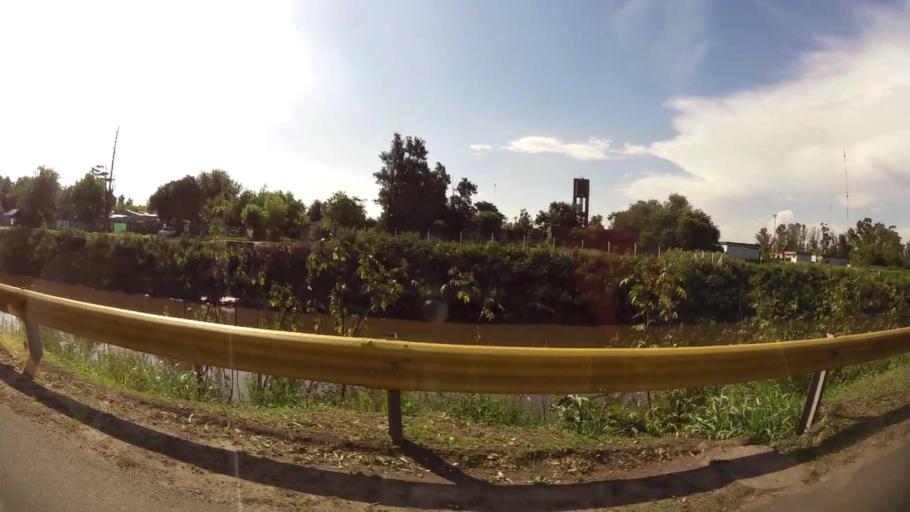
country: AR
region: Buenos Aires
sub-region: Partido de Merlo
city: Merlo
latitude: -34.6566
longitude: -58.7521
